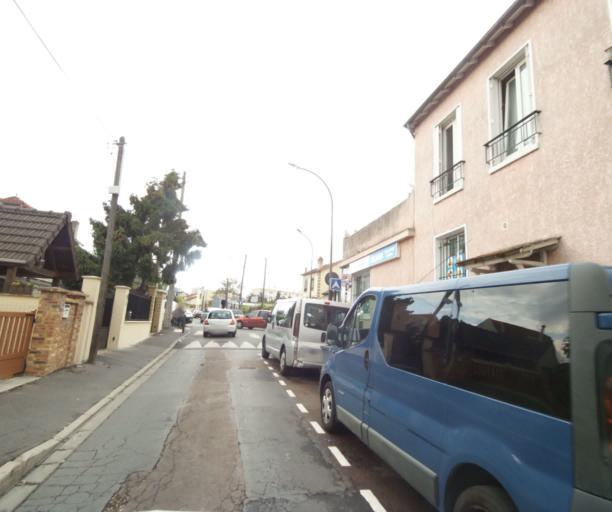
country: FR
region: Ile-de-France
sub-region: Departement du Val-d'Oise
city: Bezons
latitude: 48.9459
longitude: 2.2238
